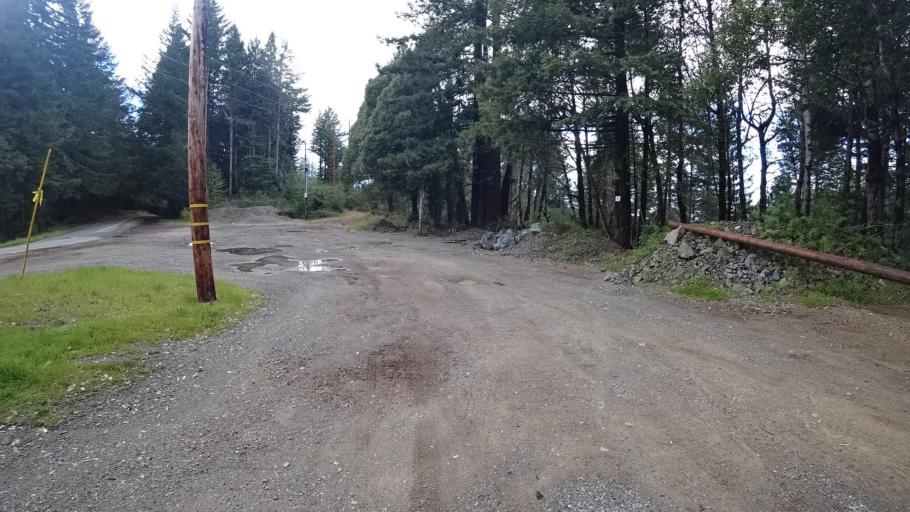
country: US
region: California
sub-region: Humboldt County
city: Bayside
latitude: 40.7486
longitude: -123.9725
